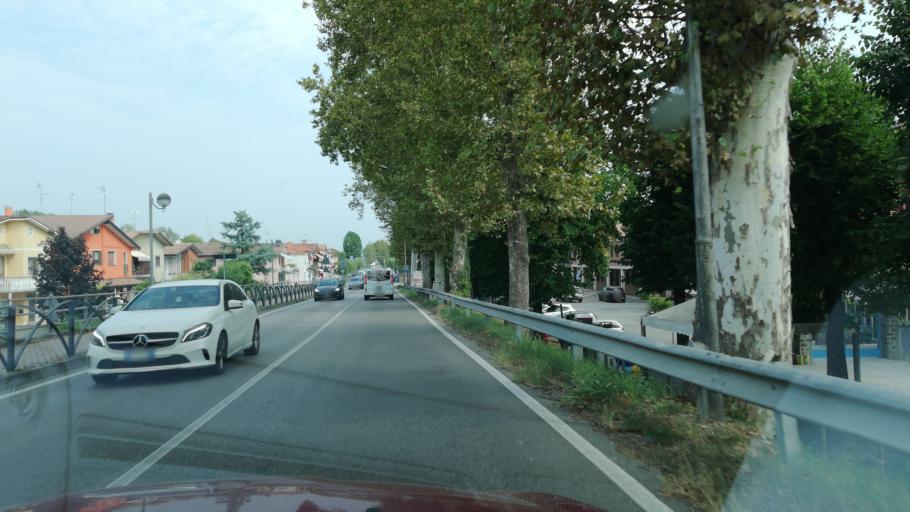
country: IT
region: Veneto
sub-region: Provincia di Venezia
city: La Salute di Livenza
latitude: 45.6570
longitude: 12.8015
